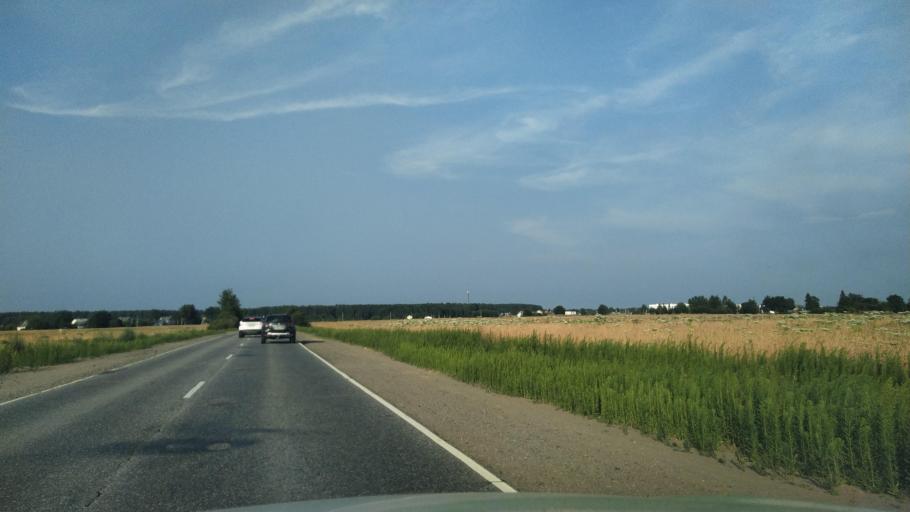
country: RU
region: Leningrad
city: Koltushi
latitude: 59.8881
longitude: 30.7227
